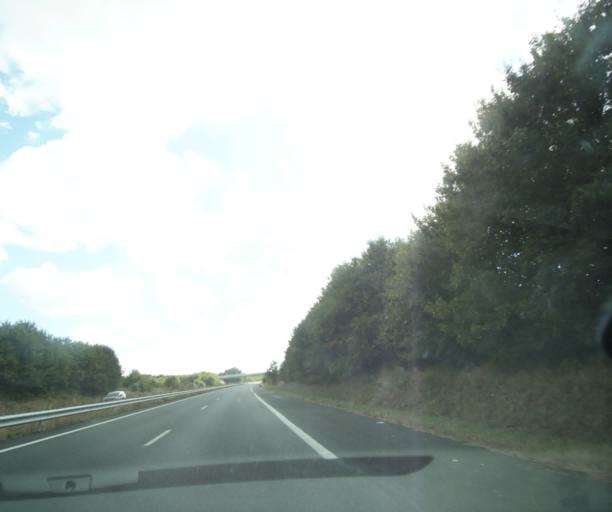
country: FR
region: Poitou-Charentes
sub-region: Departement de la Charente-Maritime
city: Bords
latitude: 45.9081
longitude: -0.7778
